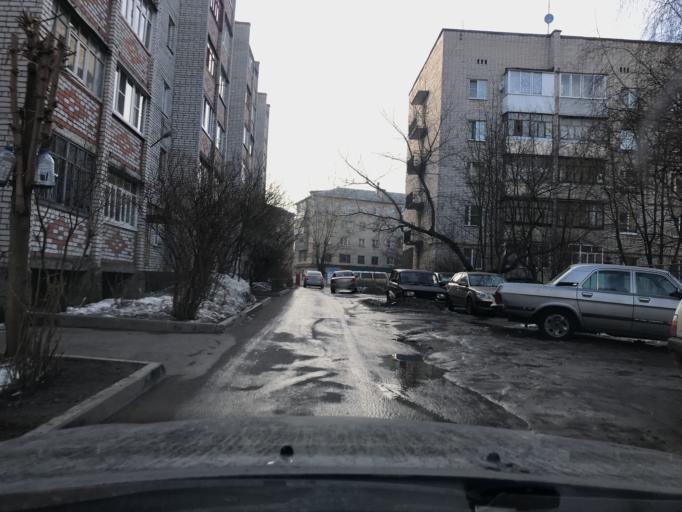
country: RU
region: Kaluga
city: Kaluga
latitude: 54.5321
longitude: 36.2643
